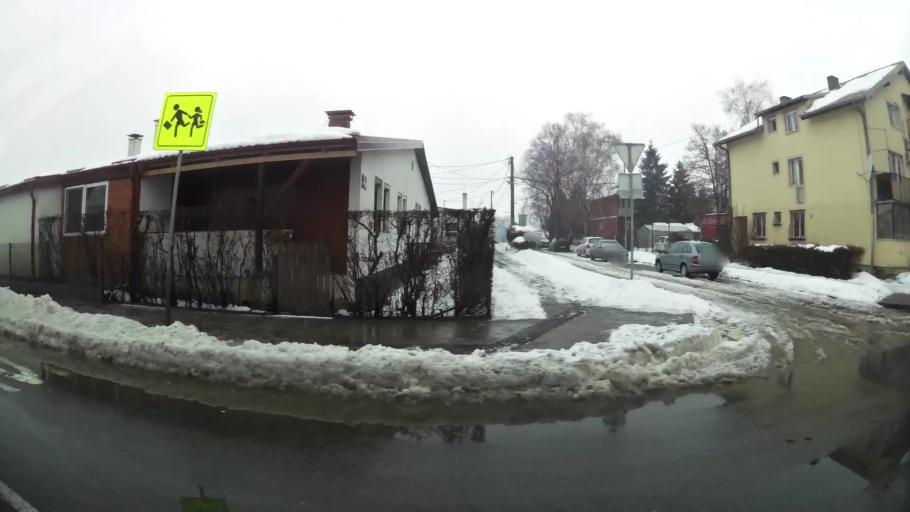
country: RS
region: Central Serbia
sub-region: Belgrade
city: Zemun
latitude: 44.8696
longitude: 20.3229
